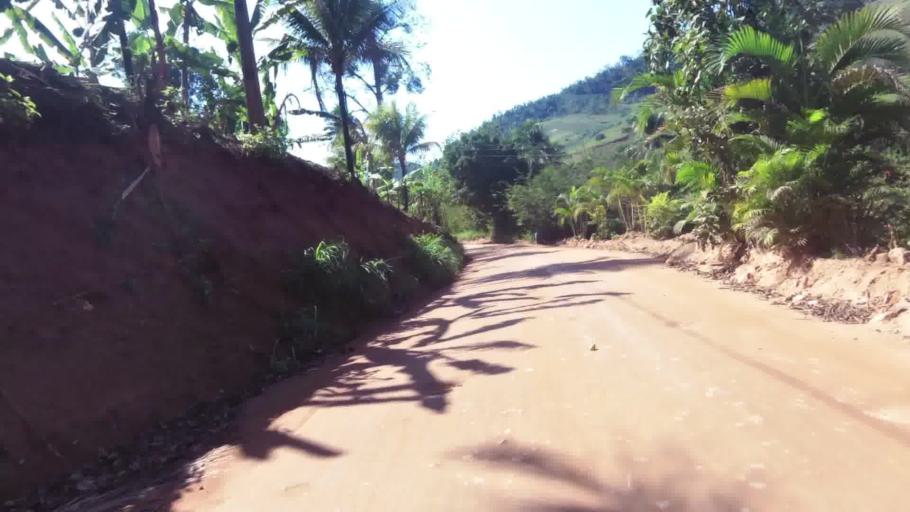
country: BR
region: Espirito Santo
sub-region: Alfredo Chaves
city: Alfredo Chaves
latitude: -20.6421
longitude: -40.7780
